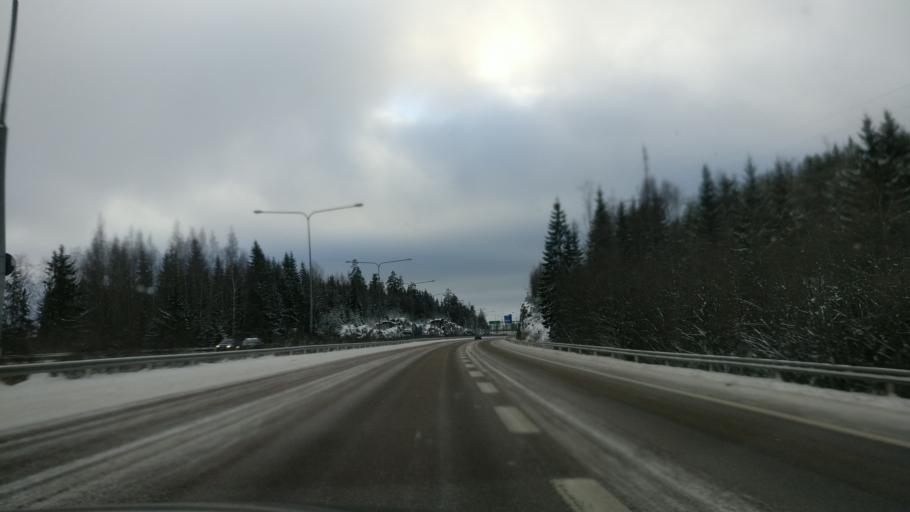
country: FI
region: Paijanne Tavastia
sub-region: Lahti
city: Lahti
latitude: 60.9771
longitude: 25.7295
